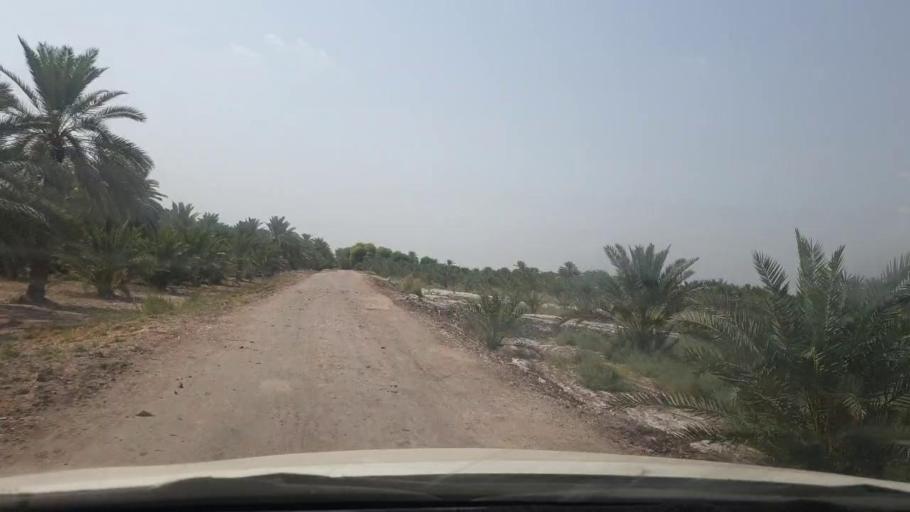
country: PK
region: Sindh
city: Khairpur
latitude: 27.5602
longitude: 68.8495
